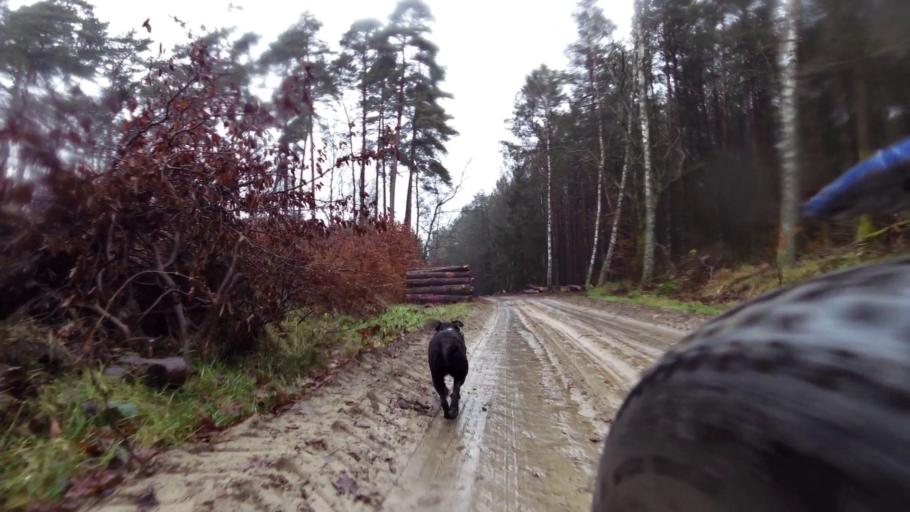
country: PL
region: West Pomeranian Voivodeship
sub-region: Powiat drawski
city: Zlocieniec
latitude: 53.5508
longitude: 15.9392
